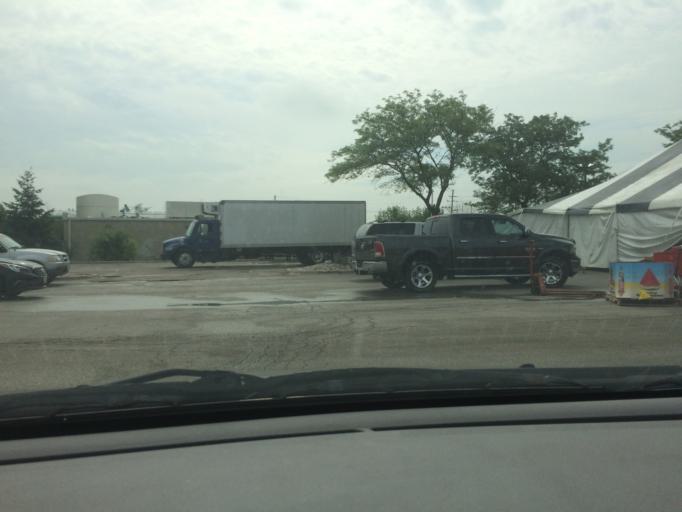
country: US
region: Illinois
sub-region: Cook County
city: Bartlett
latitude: 41.9755
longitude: -88.2085
